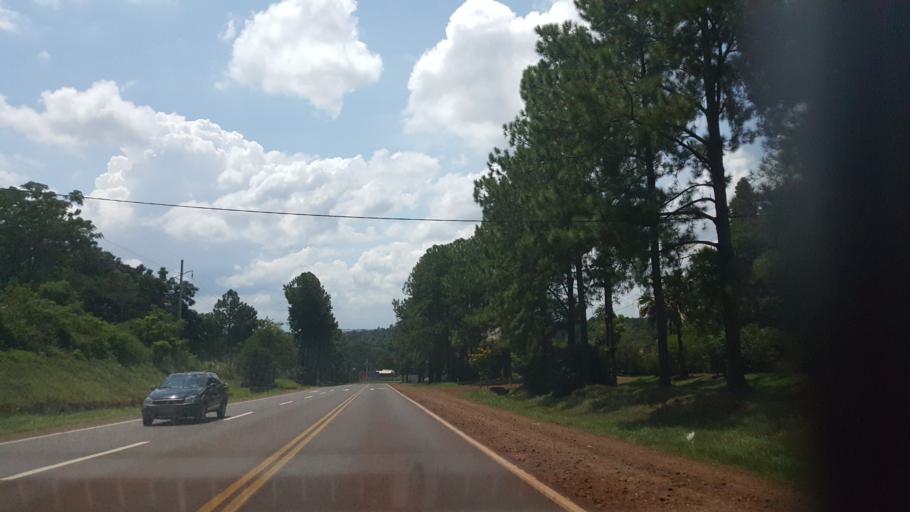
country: AR
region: Misiones
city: Puerto Rico
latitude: -26.8367
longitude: -55.0378
